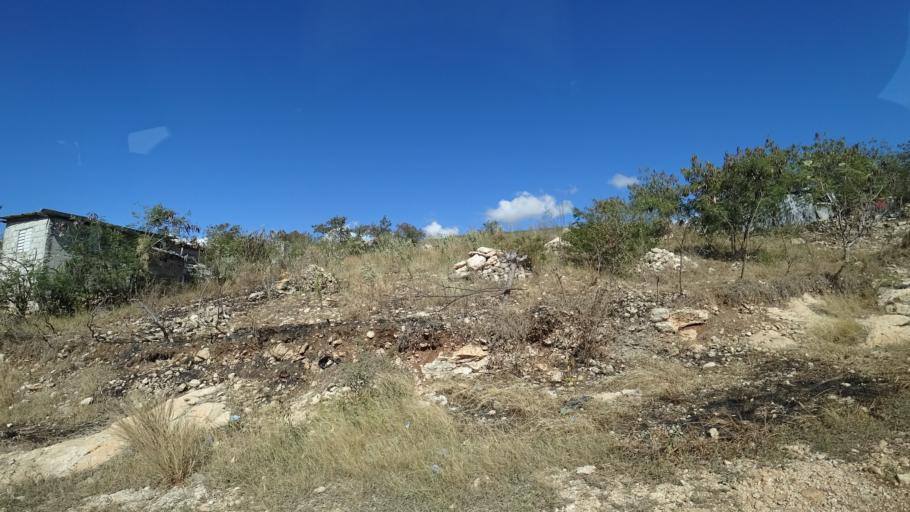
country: HT
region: Ouest
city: Croix des Bouquets
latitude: 18.6722
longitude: -72.2711
